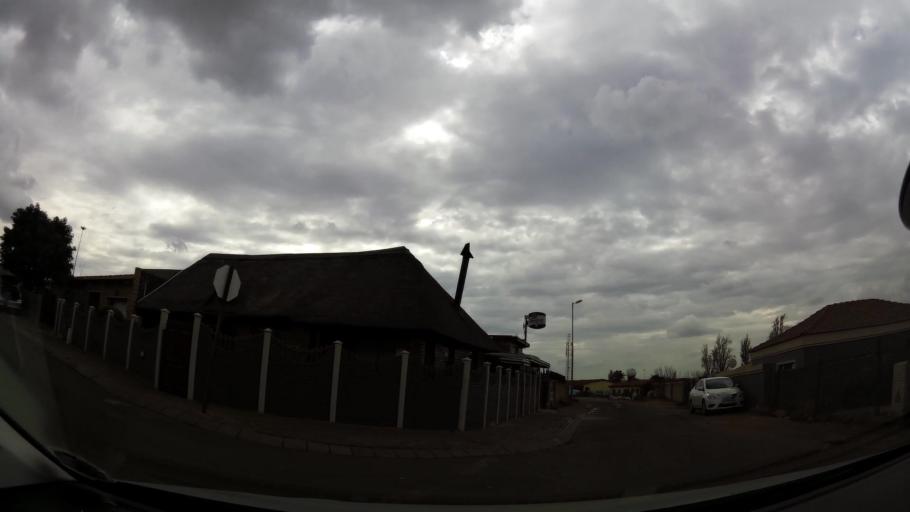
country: ZA
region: Gauteng
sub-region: City of Johannesburg Metropolitan Municipality
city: Soweto
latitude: -26.2701
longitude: 27.8743
